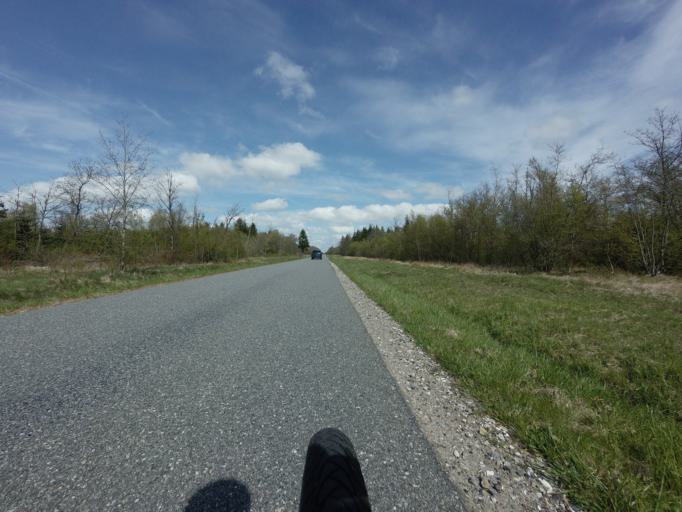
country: DK
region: North Denmark
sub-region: Jammerbugt Kommune
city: Brovst
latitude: 57.1680
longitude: 9.5434
